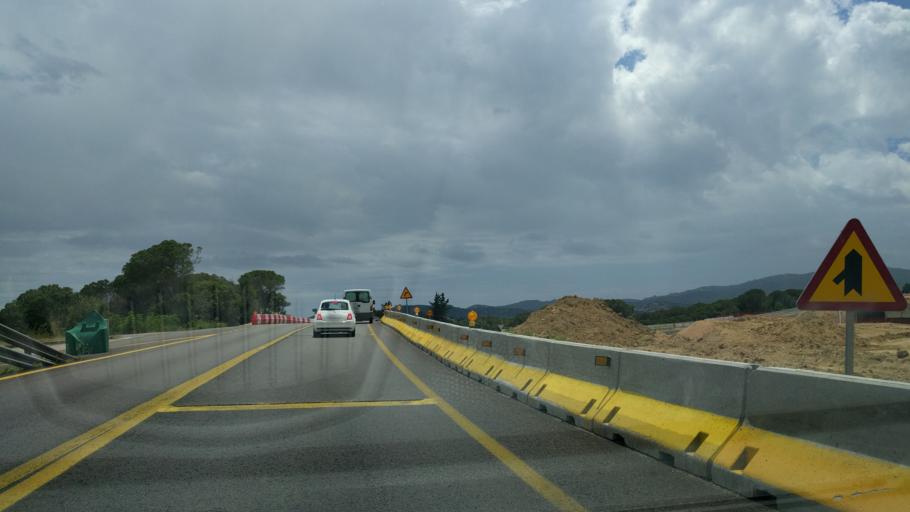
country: ES
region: Catalonia
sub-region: Provincia de Barcelona
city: Tordera
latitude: 41.7195
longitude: 2.7351
